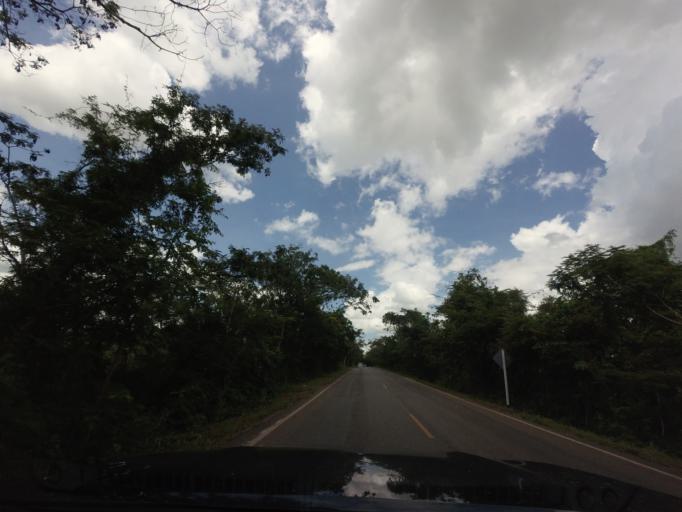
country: TH
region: Changwat Udon Thani
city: Phibun Rak
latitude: 17.6113
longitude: 103.0790
